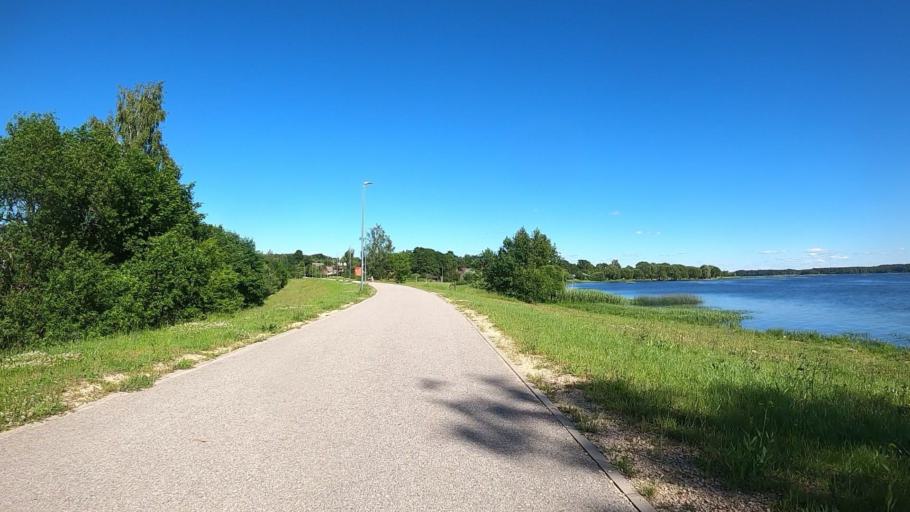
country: LV
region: Ikskile
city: Ikskile
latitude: 56.8238
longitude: 24.4940
